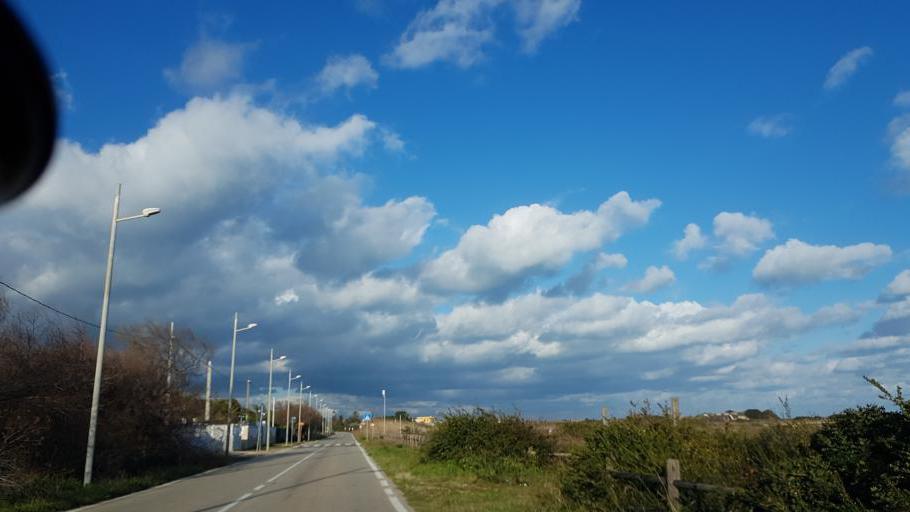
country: IT
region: Apulia
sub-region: Provincia di Brindisi
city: Materdomini
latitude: 40.6766
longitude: 17.9428
